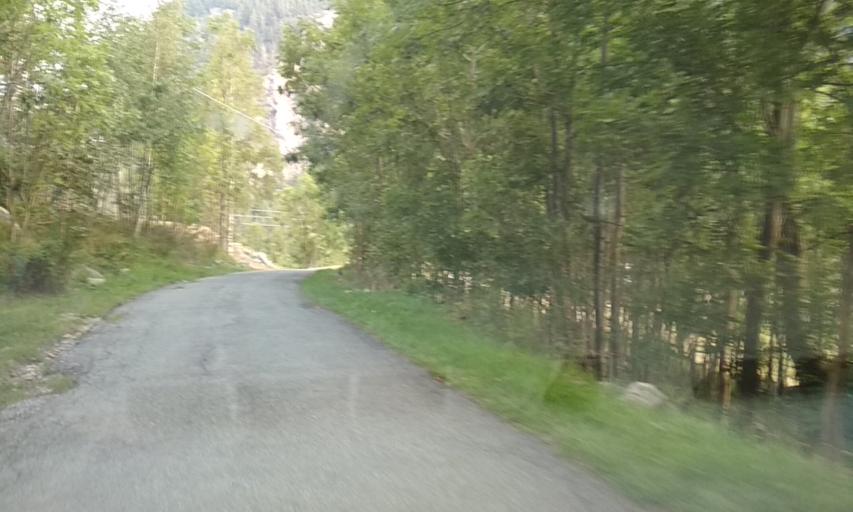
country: IT
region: Piedmont
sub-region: Provincia di Torino
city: Noasca
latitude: 45.4554
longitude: 7.3026
